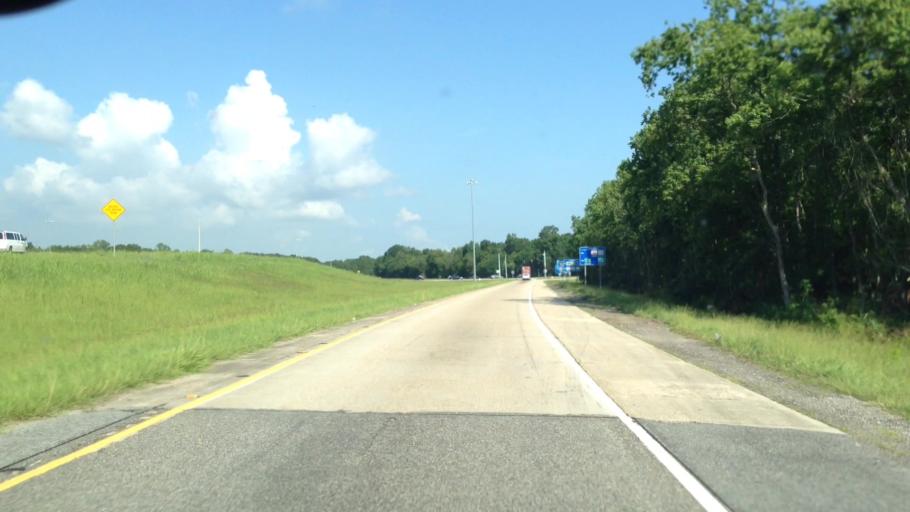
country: US
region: Louisiana
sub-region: Ascension Parish
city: Sorrento
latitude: 30.1709
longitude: -90.8732
